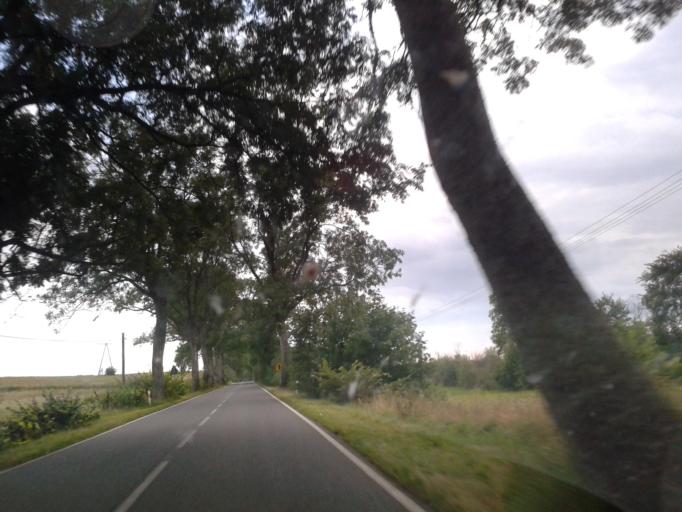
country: PL
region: West Pomeranian Voivodeship
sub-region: Powiat szczecinecki
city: Grzmiaca
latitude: 53.8771
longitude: 16.4955
